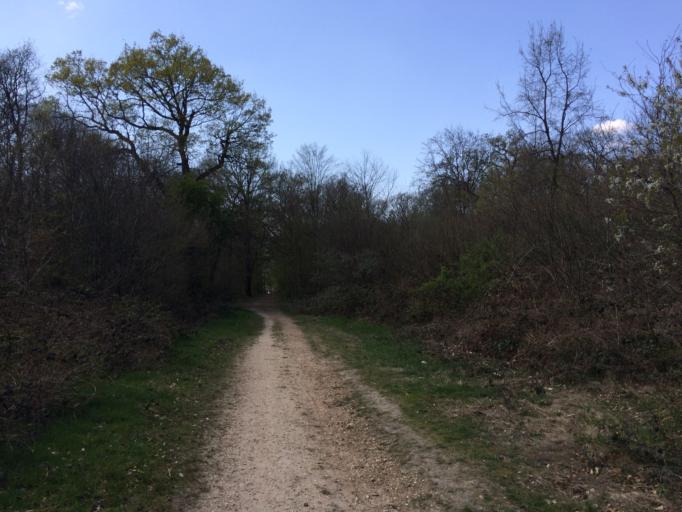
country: FR
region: Ile-de-France
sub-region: Departement de l'Essonne
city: Draveil
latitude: 48.6727
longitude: 2.4211
